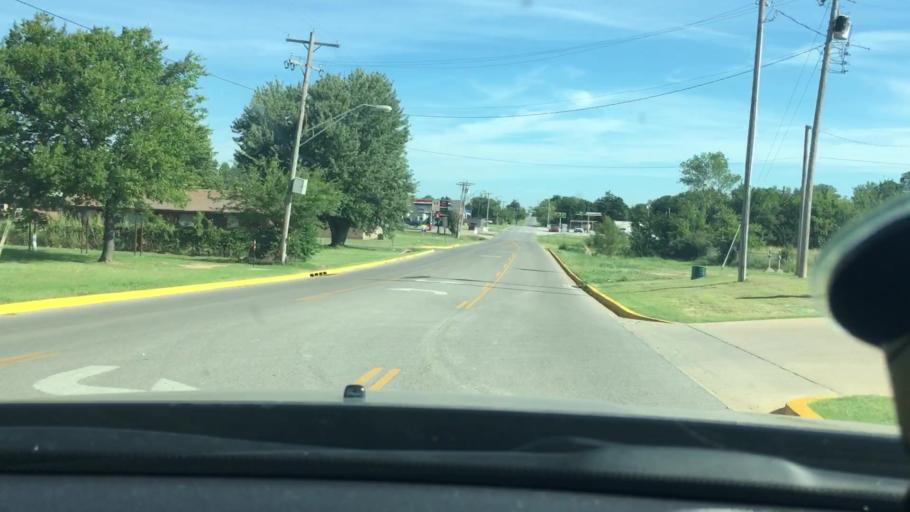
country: US
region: Oklahoma
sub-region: Carter County
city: Lone Grove
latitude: 34.1789
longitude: -97.2474
